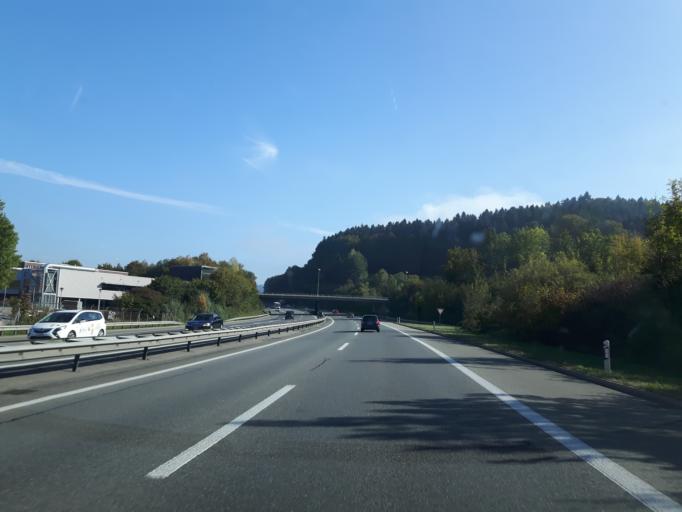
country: CH
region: Lucerne
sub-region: Willisau District
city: Dagmersellen
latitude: 47.2094
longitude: 7.9807
